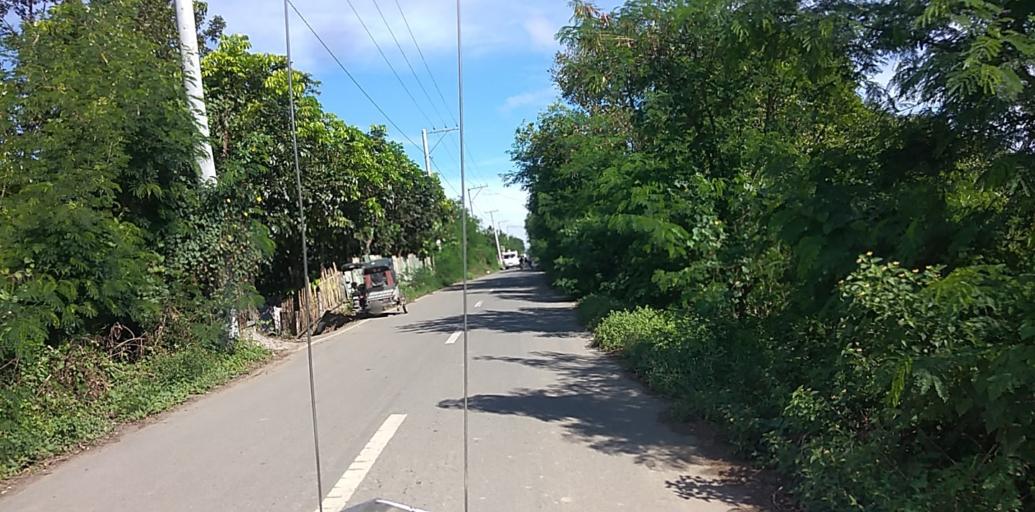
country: PH
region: Central Luzon
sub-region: Province of Pampanga
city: San Nicolas
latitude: 15.0710
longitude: 120.8061
